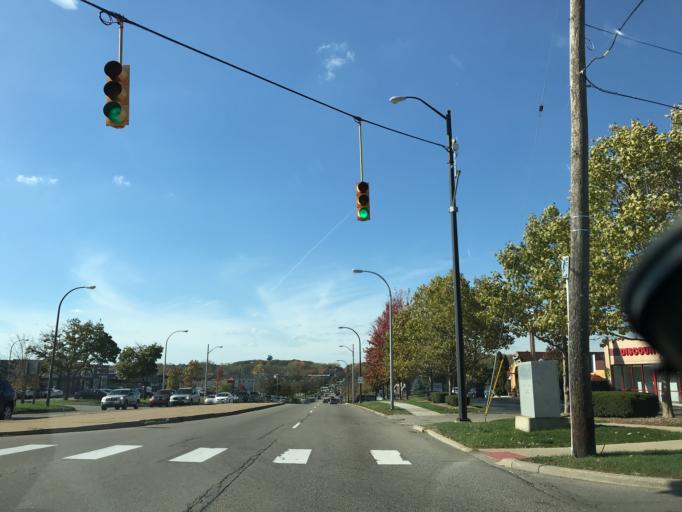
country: US
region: Michigan
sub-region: Washtenaw County
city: Ann Arbor
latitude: 42.2558
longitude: -83.6902
